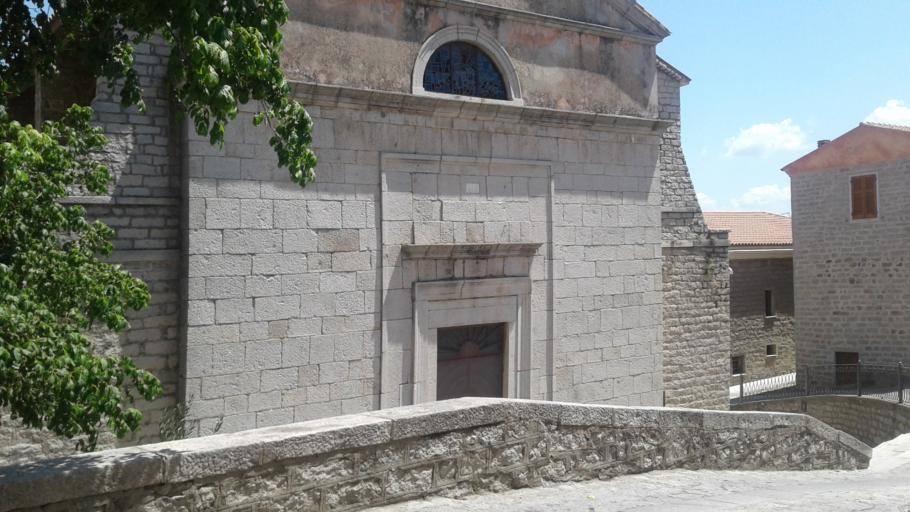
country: IT
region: Sardinia
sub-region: Provincia di Olbia-Tempio
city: Aggius
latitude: 40.9300
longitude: 9.0649
